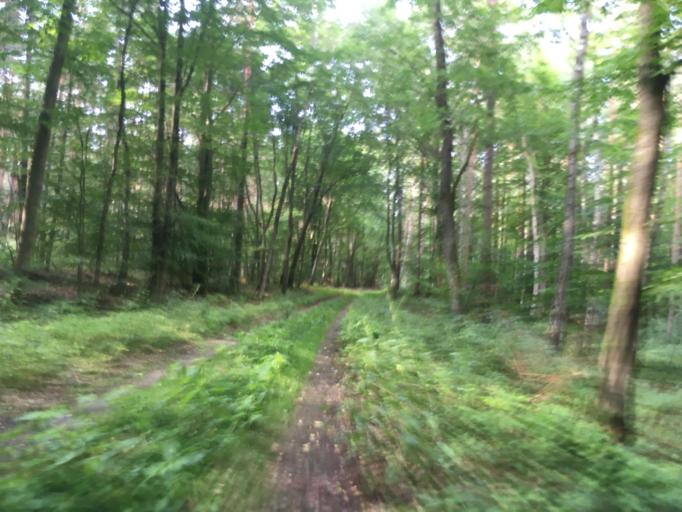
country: DE
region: Brandenburg
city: Eberswalde
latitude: 52.7984
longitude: 13.8199
